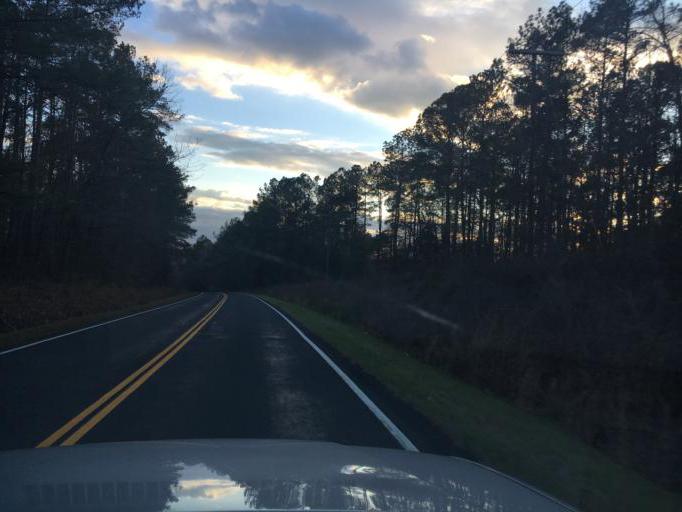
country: US
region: South Carolina
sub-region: Greenwood County
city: Greenwood
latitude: 34.0786
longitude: -82.2173
